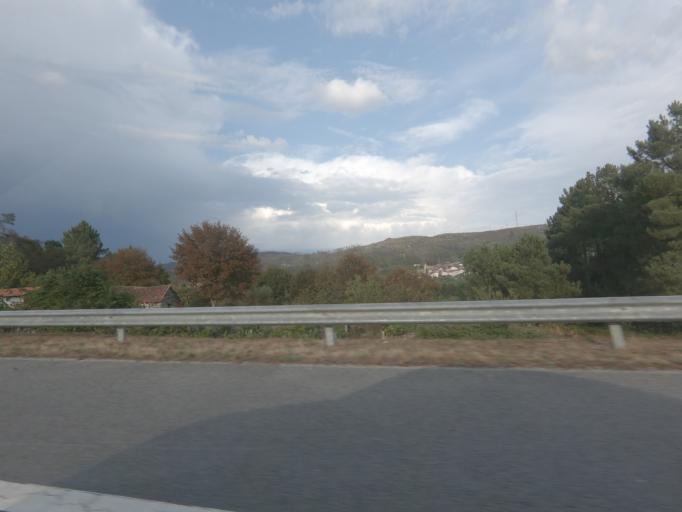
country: PT
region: Viseu
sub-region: Castro Daire
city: Castro Daire
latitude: 40.8445
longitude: -7.9267
